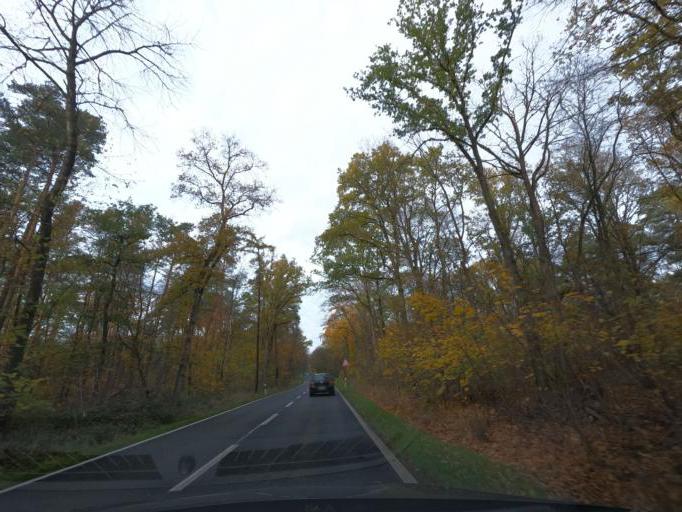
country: DE
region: Lower Saxony
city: Braunschweig
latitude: 52.3072
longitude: 10.5696
